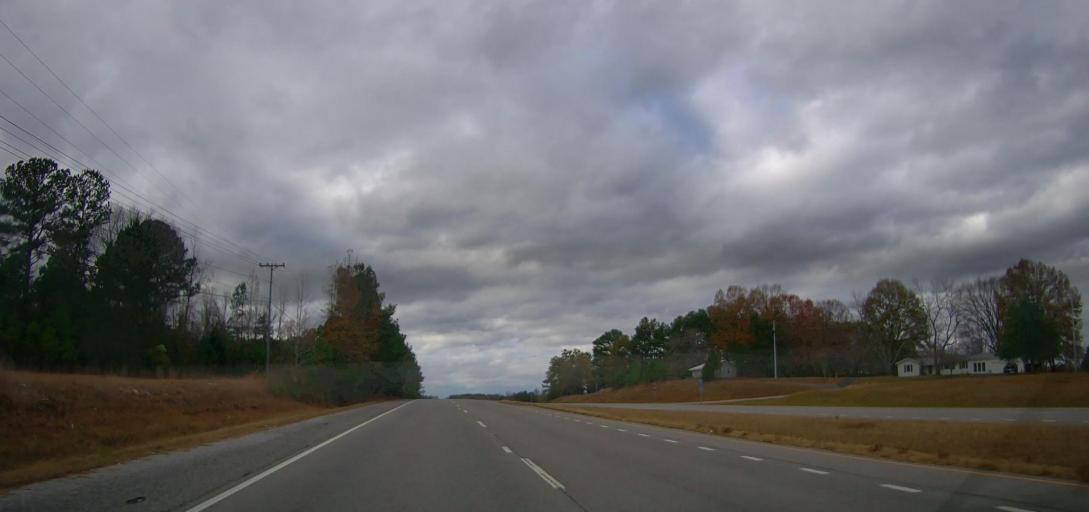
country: US
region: Alabama
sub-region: Lawrence County
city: Town Creek
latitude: 34.5775
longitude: -87.4051
